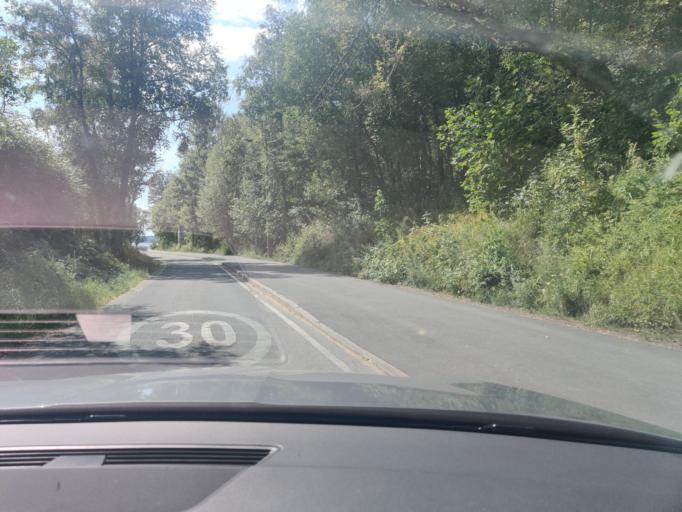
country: EE
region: Harju
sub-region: Harku vald
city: Tabasalu
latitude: 59.4608
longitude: 24.5720
